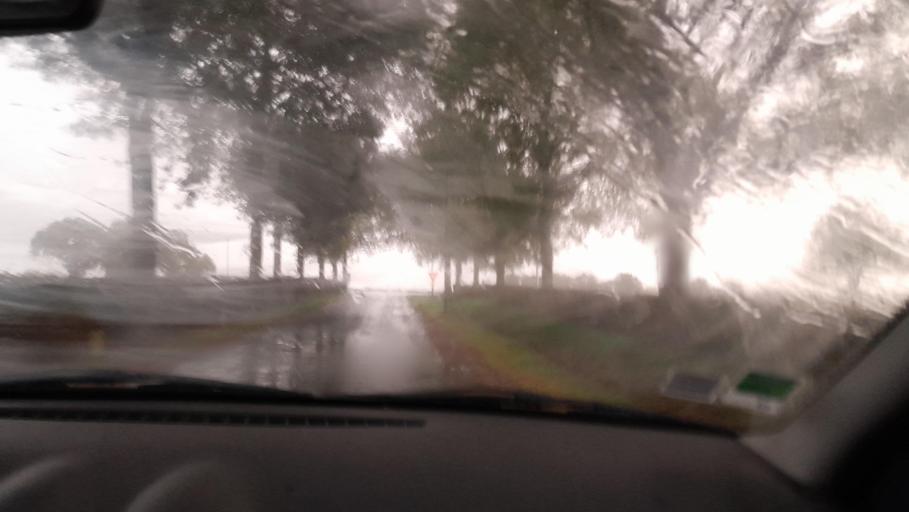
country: FR
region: Pays de la Loire
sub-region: Departement de la Mayenne
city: Ballots
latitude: 47.8610
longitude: -1.0686
